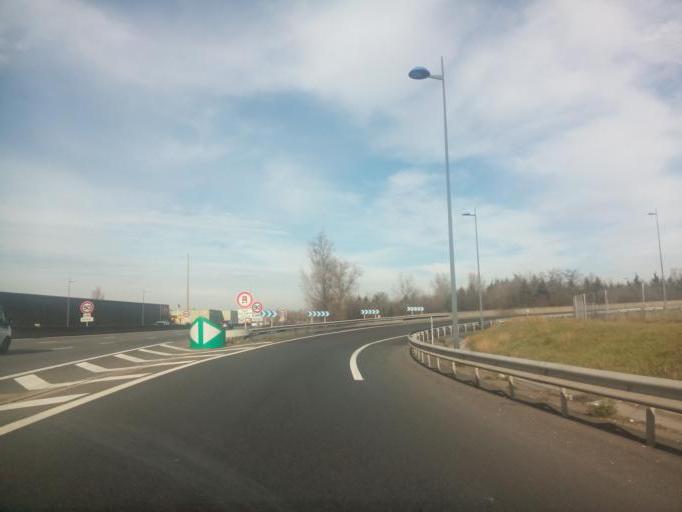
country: FR
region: Rhone-Alpes
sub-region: Departement du Rhone
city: Pierre-Benite
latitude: 45.6990
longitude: 4.8361
